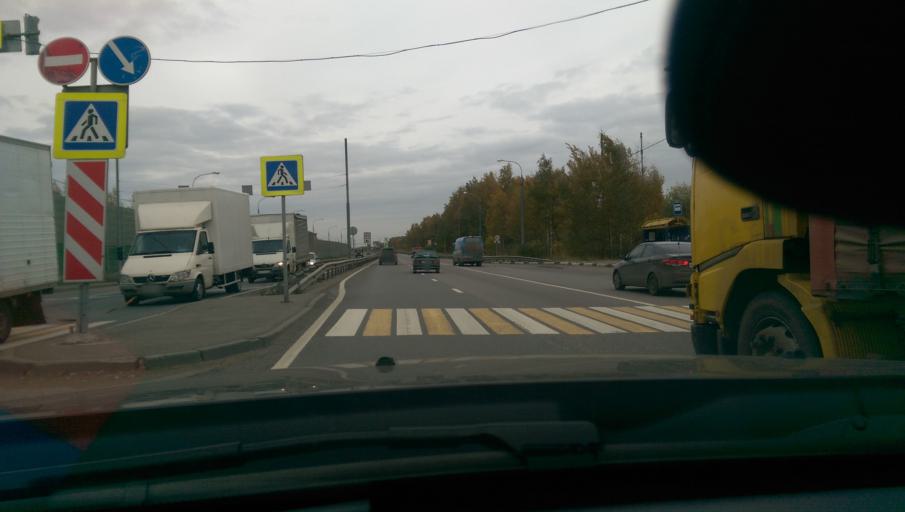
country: RU
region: Moskovskaya
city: Povedniki
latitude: 55.9460
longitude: 37.6546
